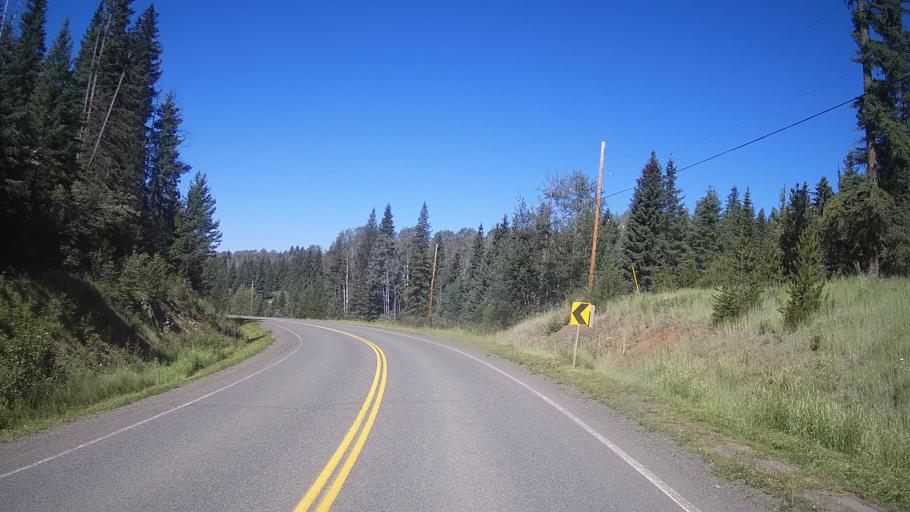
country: CA
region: British Columbia
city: Kamloops
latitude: 51.5057
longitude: -120.6042
